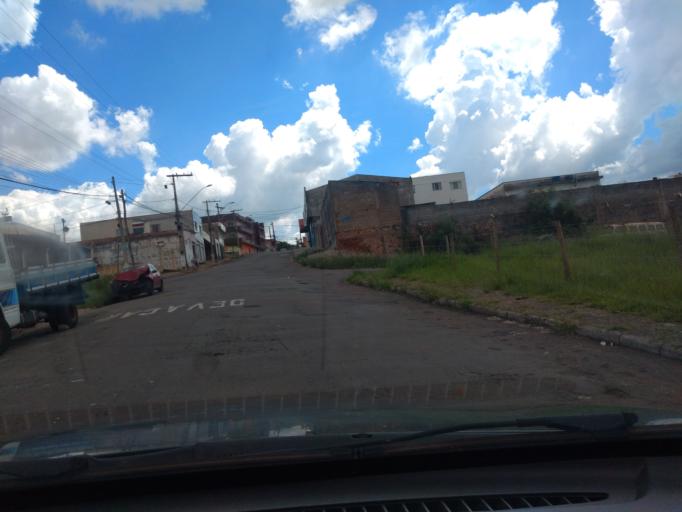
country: BR
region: Minas Gerais
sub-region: Tres Coracoes
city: Tres Coracoes
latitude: -21.6847
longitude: -45.2617
